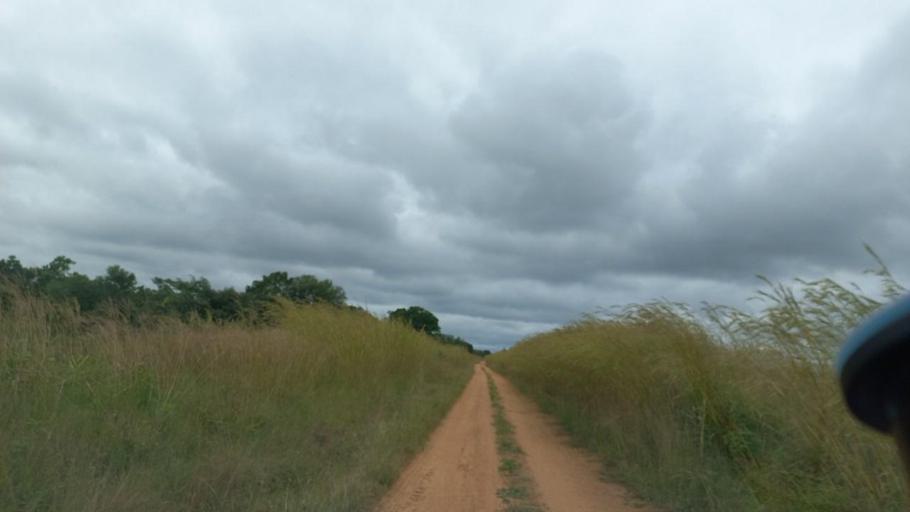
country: ZM
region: Lusaka
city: Lusaka
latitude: -15.1309
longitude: 28.3695
